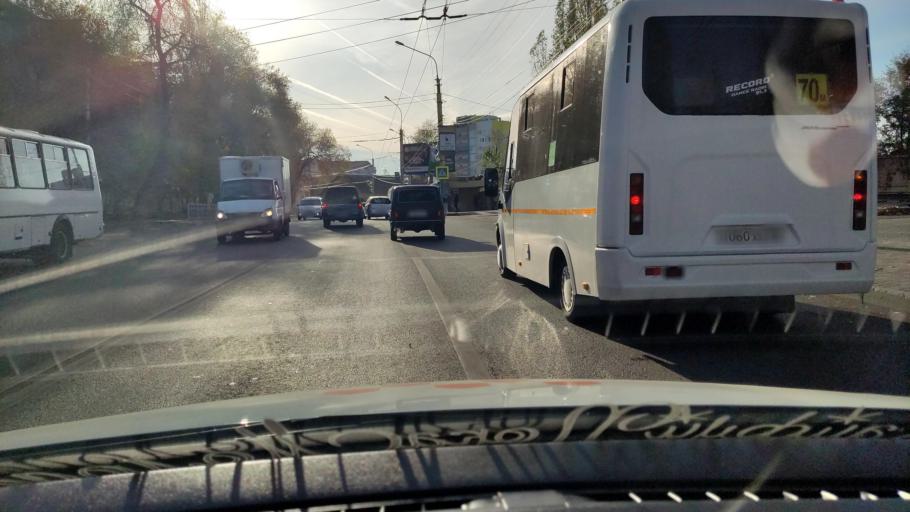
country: RU
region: Voronezj
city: Voronezh
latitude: 51.6501
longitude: 39.1526
